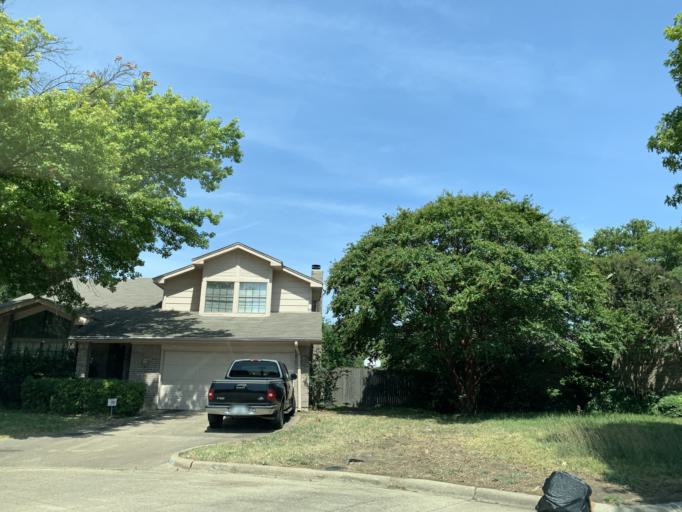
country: US
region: Texas
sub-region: Dallas County
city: Grand Prairie
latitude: 32.6632
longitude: -97.0405
